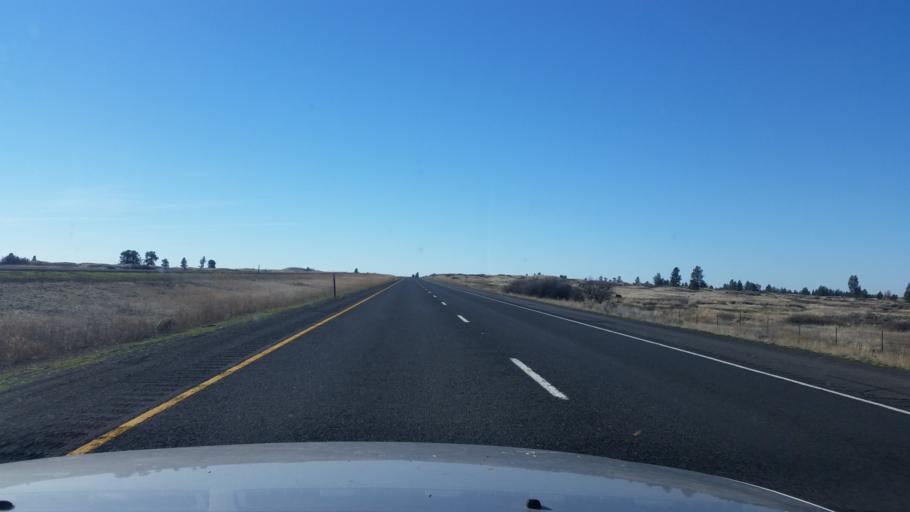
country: US
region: Washington
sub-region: Spokane County
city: Medical Lake
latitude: 47.3905
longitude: -117.8497
